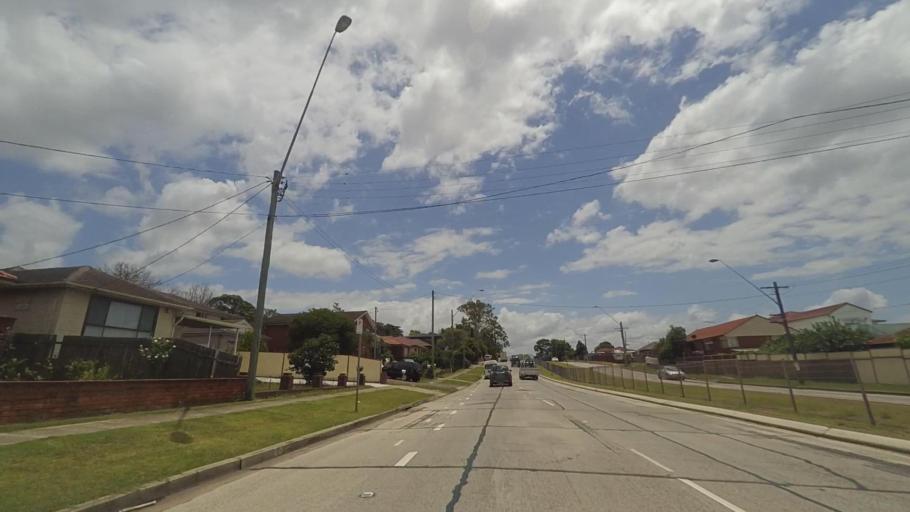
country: AU
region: New South Wales
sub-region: Fairfield
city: Cabramatta West
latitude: -33.8874
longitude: 150.9230
